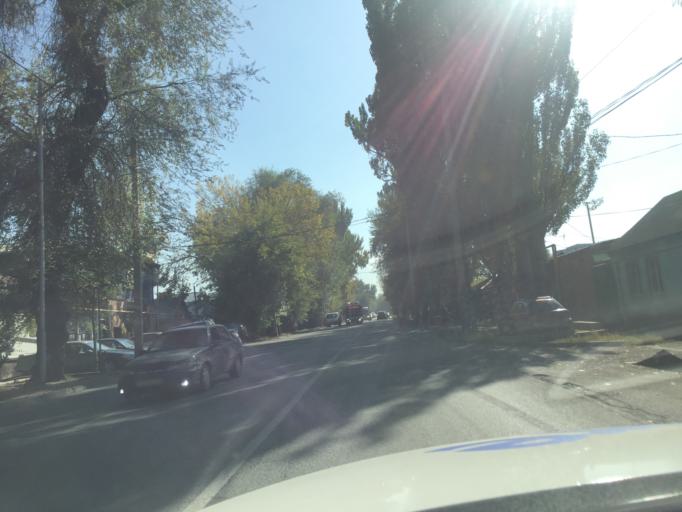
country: KZ
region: Almaty Qalasy
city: Almaty
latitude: 43.2631
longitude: 76.9107
